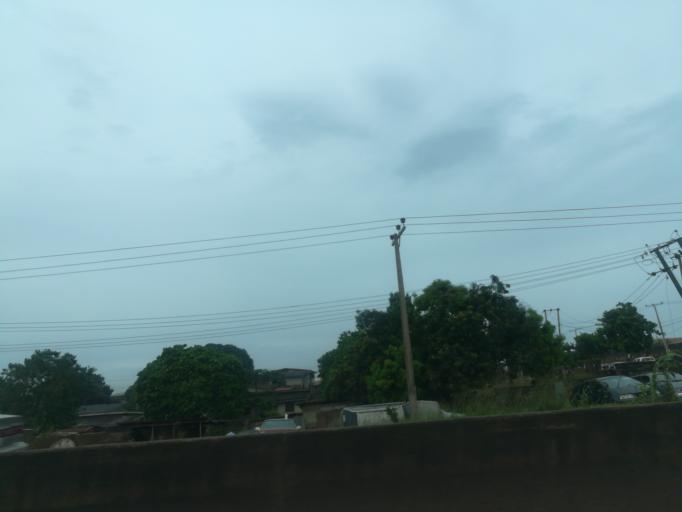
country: NG
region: Oyo
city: Ibadan
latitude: 7.3946
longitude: 3.9618
